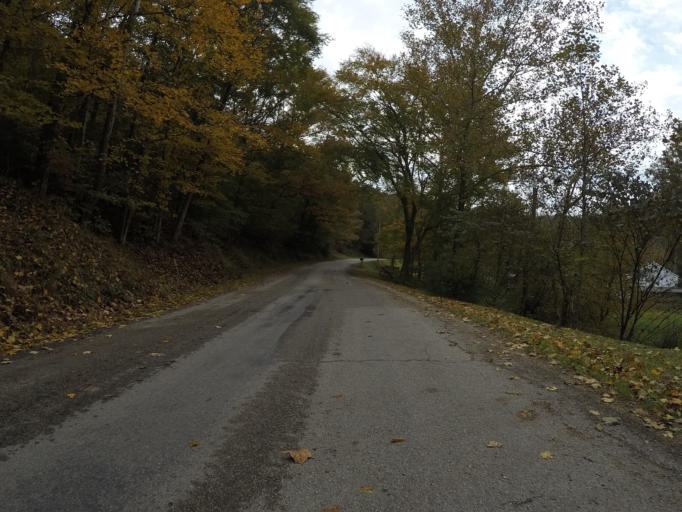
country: US
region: West Virginia
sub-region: Wayne County
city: Lavalette
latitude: 38.3372
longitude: -82.4385
